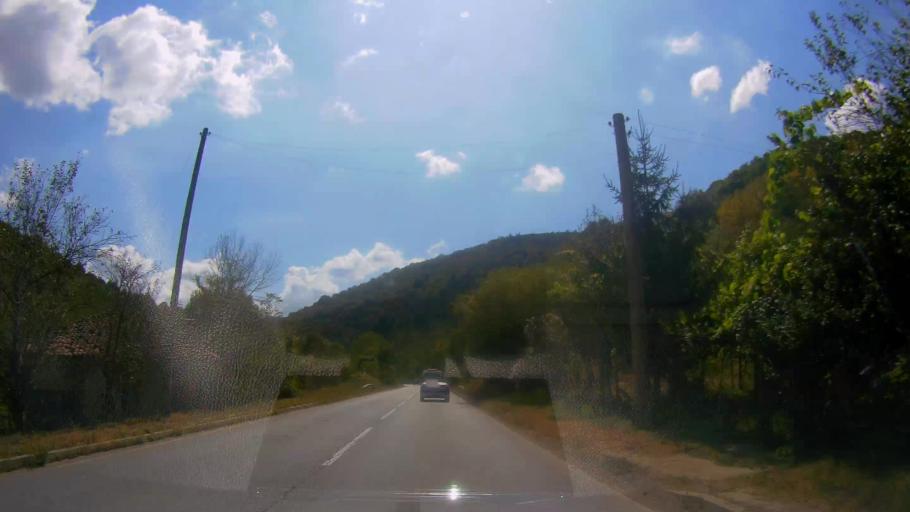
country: BG
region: Stara Zagora
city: Gurkovo
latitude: 42.7385
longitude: 25.7079
